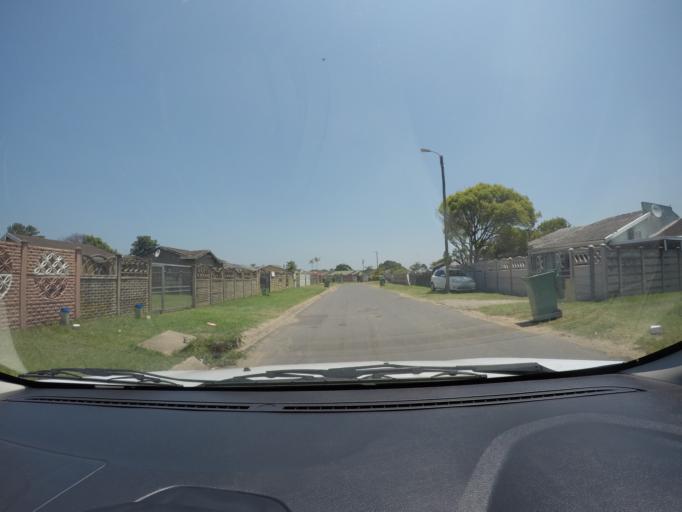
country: ZA
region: KwaZulu-Natal
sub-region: uThungulu District Municipality
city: eSikhawini
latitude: -28.8873
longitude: 31.8892
